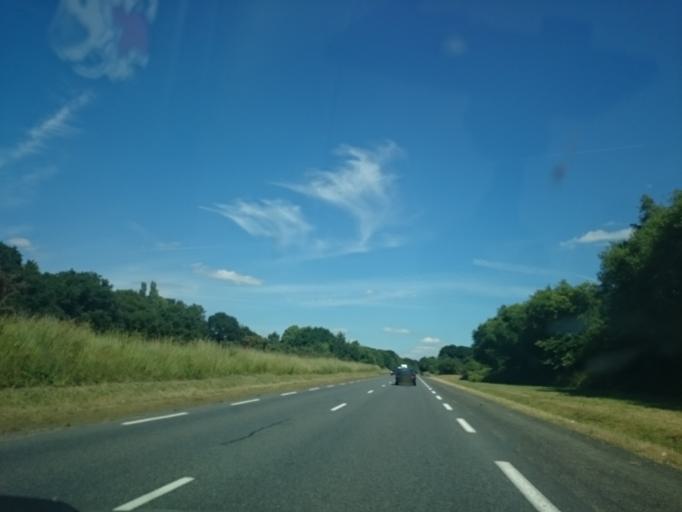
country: FR
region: Brittany
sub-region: Departement des Cotes-d'Armor
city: Plouguernevel
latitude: 48.2447
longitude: -3.2478
